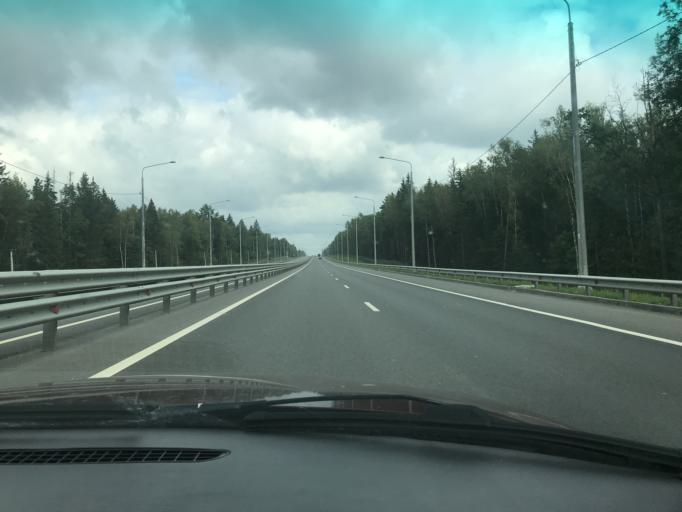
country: RU
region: Kaluga
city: Pyatovskiy
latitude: 54.6829
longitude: 36.1513
